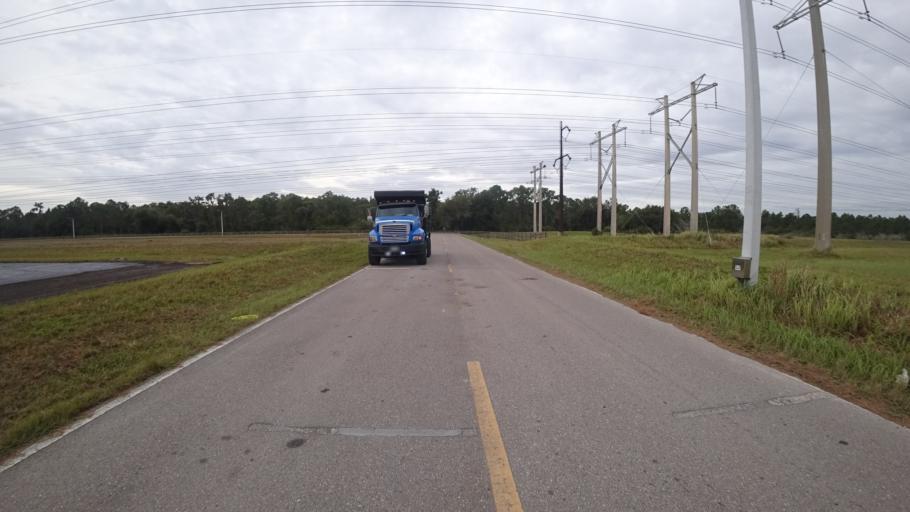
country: US
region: Florida
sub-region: Hillsborough County
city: Sun City Center
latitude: 27.6022
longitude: -82.3471
